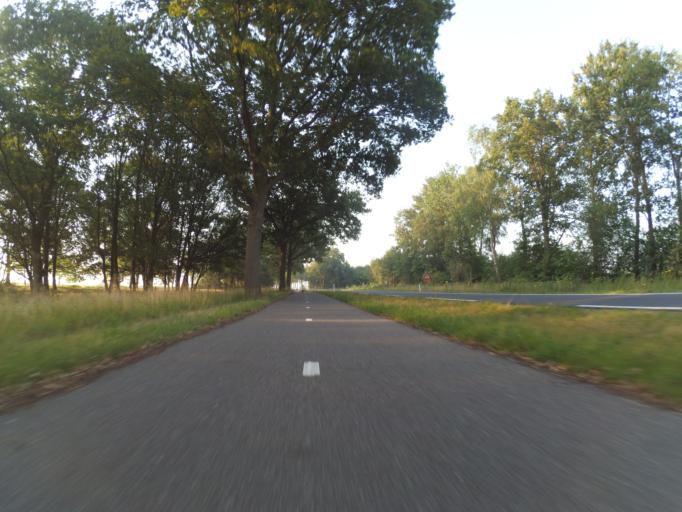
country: NL
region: Overijssel
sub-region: Gemeente Twenterand
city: Vriezenveen
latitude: 52.4257
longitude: 6.5891
